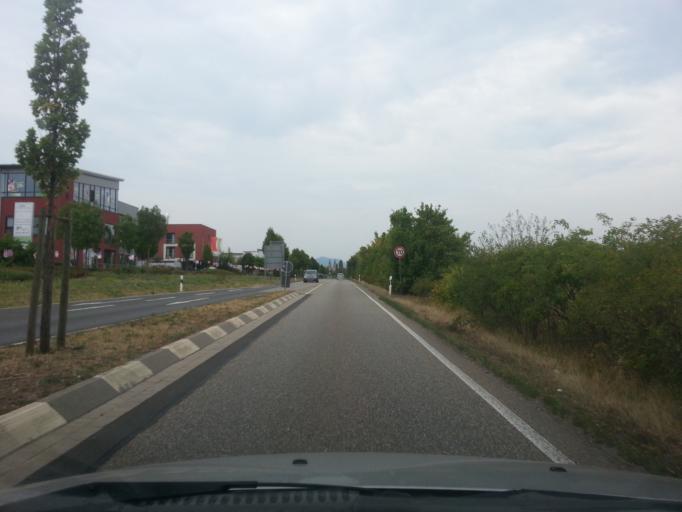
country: DE
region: Rheinland-Pfalz
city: Landau in der Pfalz
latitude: 49.1929
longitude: 8.1382
